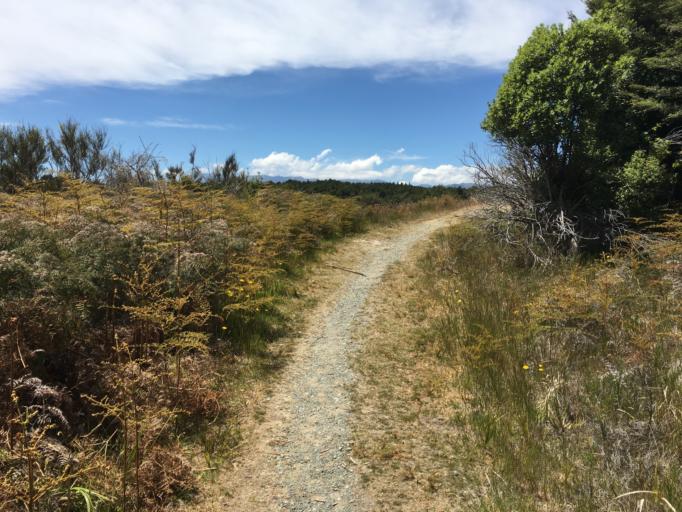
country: NZ
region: Southland
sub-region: Southland District
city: Te Anau
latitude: -45.2018
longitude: 167.8263
